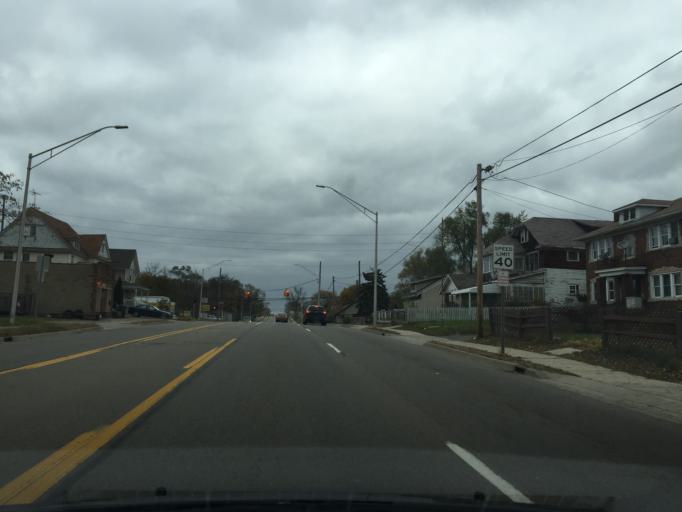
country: US
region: Michigan
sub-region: Oakland County
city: Pontiac
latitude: 42.6458
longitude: -83.3004
